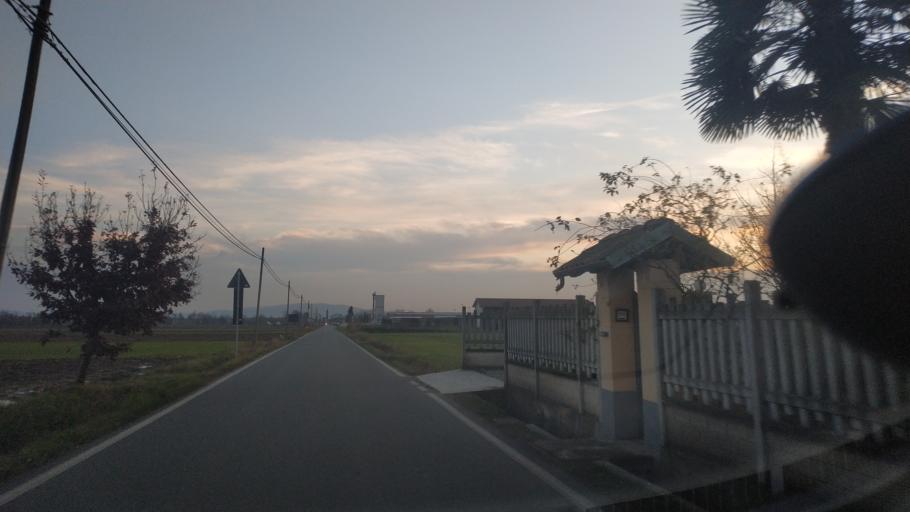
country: IT
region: Piedmont
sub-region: Provincia di Torino
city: Caluso
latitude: 45.2773
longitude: 7.8778
